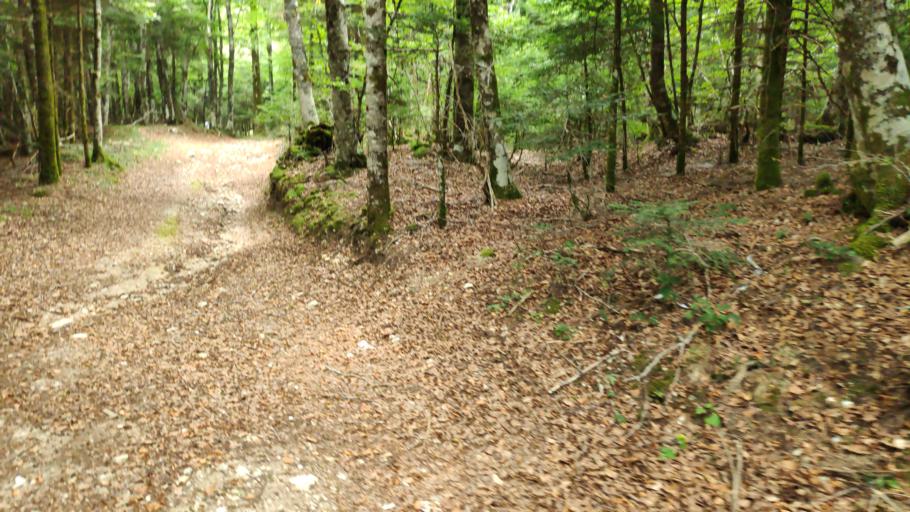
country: IT
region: Calabria
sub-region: Provincia di Vibo-Valentia
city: Serra San Bruno
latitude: 38.5425
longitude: 16.3649
